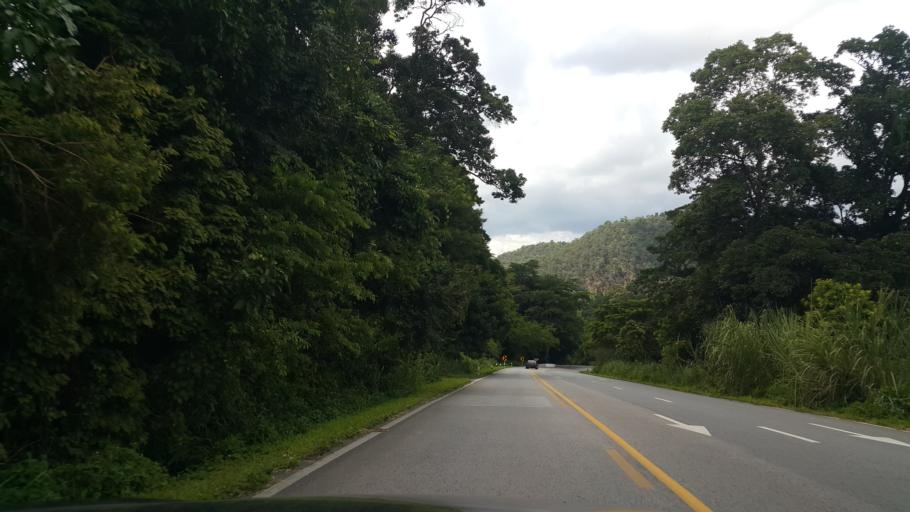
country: TH
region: Chiang Mai
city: Mae On
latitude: 18.9576
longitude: 99.2346
